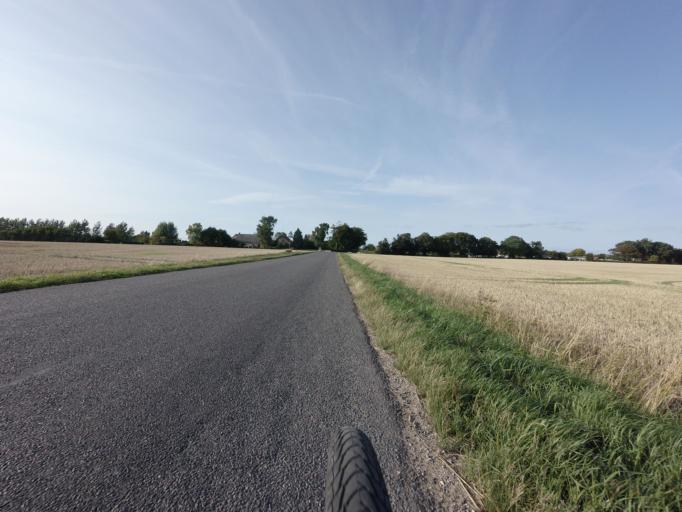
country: DK
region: Zealand
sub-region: Stevns Kommune
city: Store Heddinge
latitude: 55.2440
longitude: 12.3503
